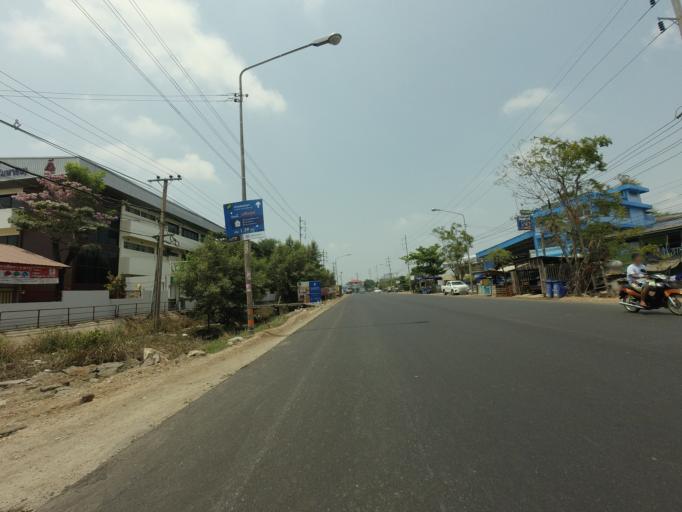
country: TH
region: Samut Prakan
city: Phra Samut Chedi
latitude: 13.5800
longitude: 100.5762
